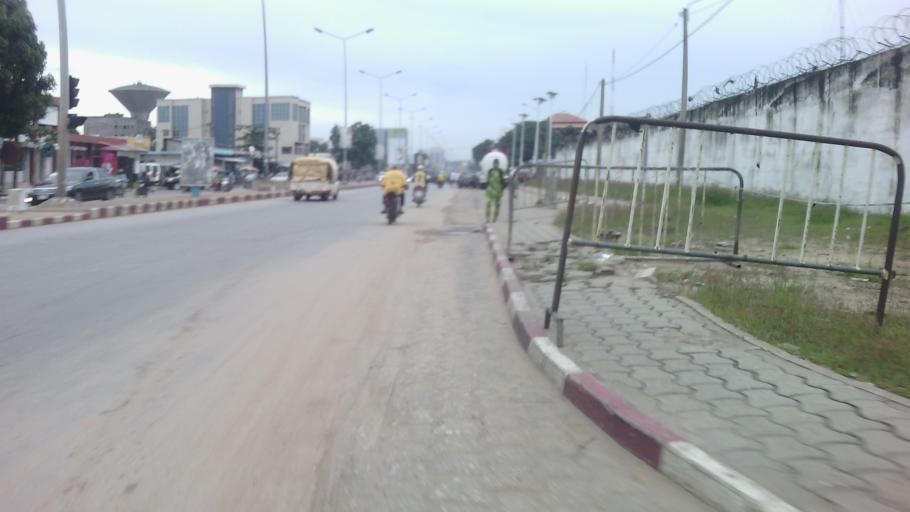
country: BJ
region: Littoral
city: Cotonou
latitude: 6.3632
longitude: 2.4193
